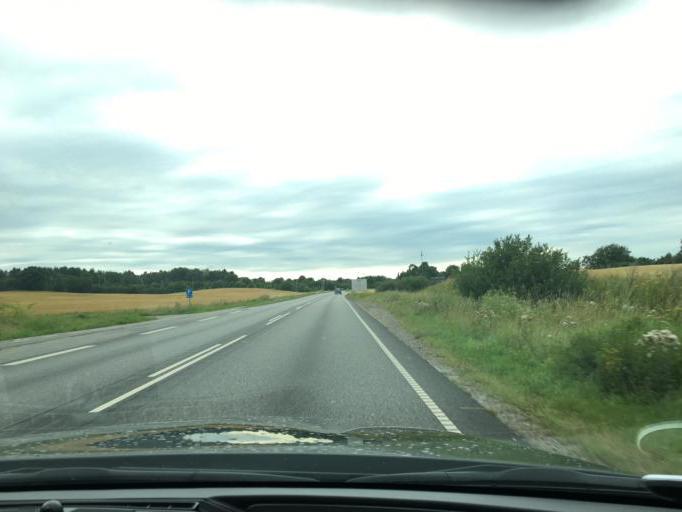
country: DK
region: Capital Region
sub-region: Horsholm Kommune
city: Horsholm
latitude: 55.8808
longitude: 12.4600
